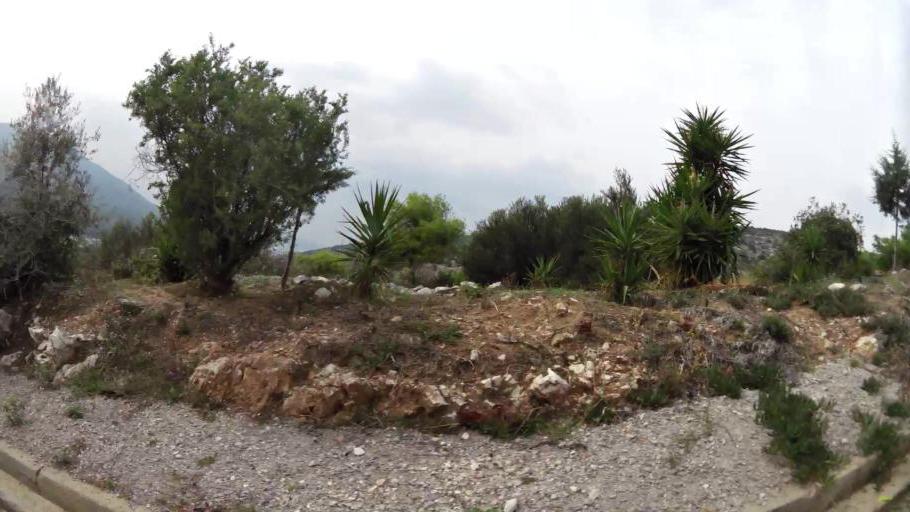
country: GR
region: Attica
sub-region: Nomarchia Athinas
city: Chaidari
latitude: 38.0198
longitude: 23.6414
